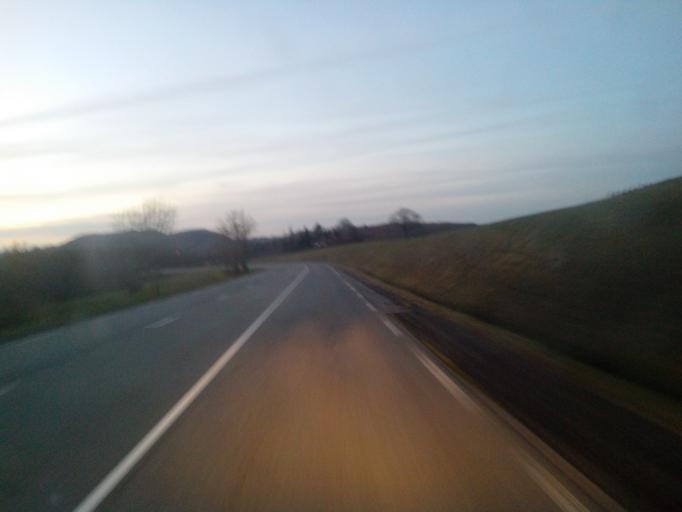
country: FR
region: Midi-Pyrenees
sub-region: Departement de l'Ariege
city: Foix
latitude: 42.9976
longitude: 1.5430
